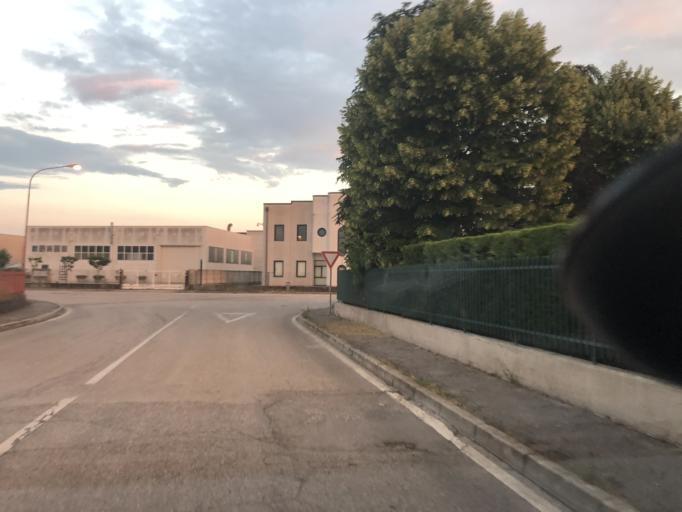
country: IT
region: Veneto
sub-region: Provincia di Verona
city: Lugagnano
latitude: 45.4486
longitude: 10.8661
